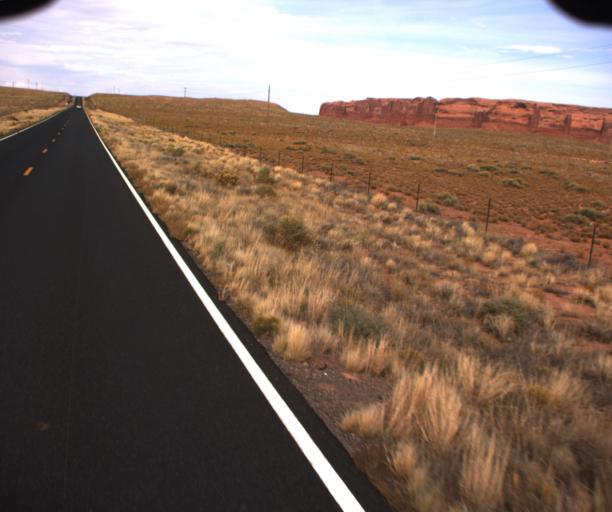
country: US
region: Arizona
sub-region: Apache County
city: Many Farms
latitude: 36.5924
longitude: -109.5634
